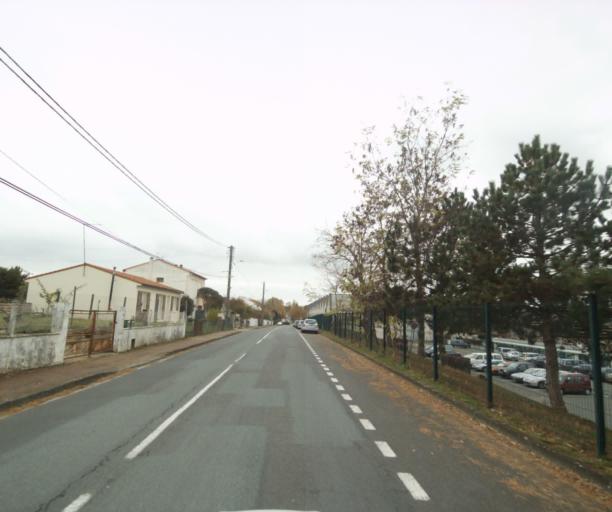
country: FR
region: Poitou-Charentes
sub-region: Departement de la Charente-Maritime
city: Saintes
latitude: 45.7509
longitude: -0.6139
